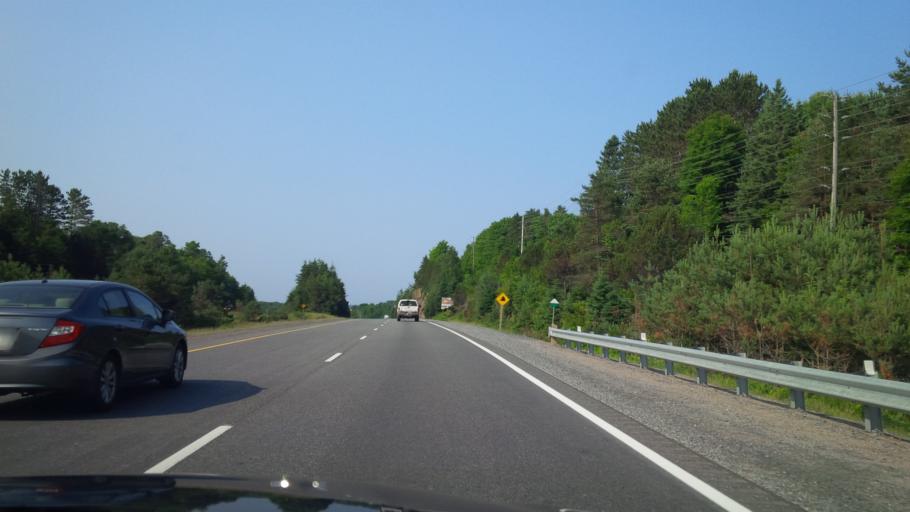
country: CA
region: Ontario
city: Huntsville
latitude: 45.2883
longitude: -79.2704
